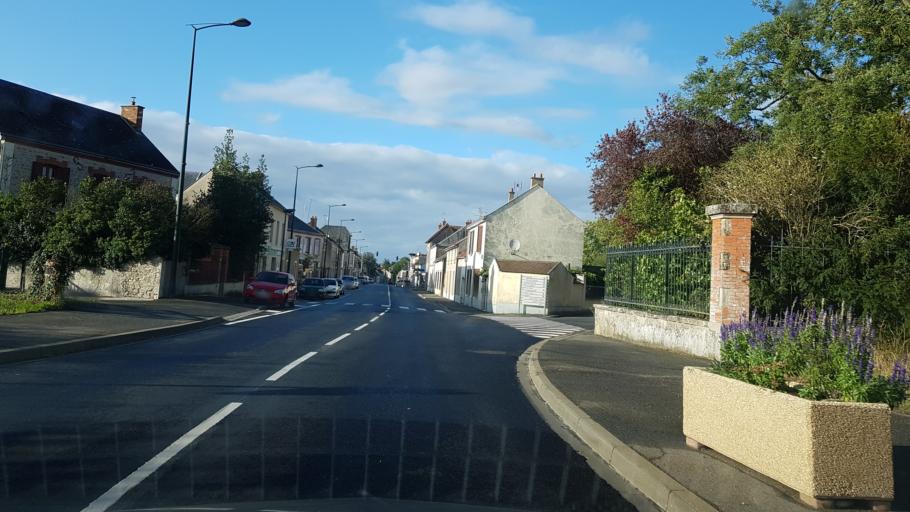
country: FR
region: Centre
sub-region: Departement du Loiret
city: Sermaises
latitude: 48.2939
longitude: 2.2023
